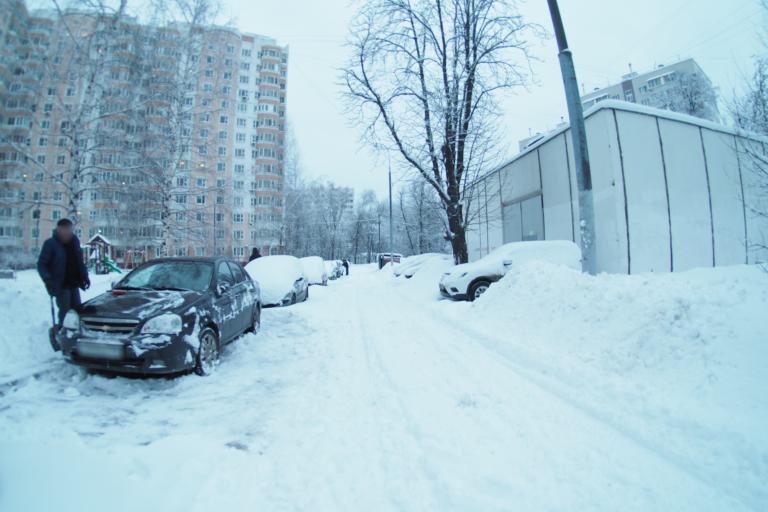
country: RU
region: Moscow
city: Ryazanskiy
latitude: 55.7418
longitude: 37.7706
